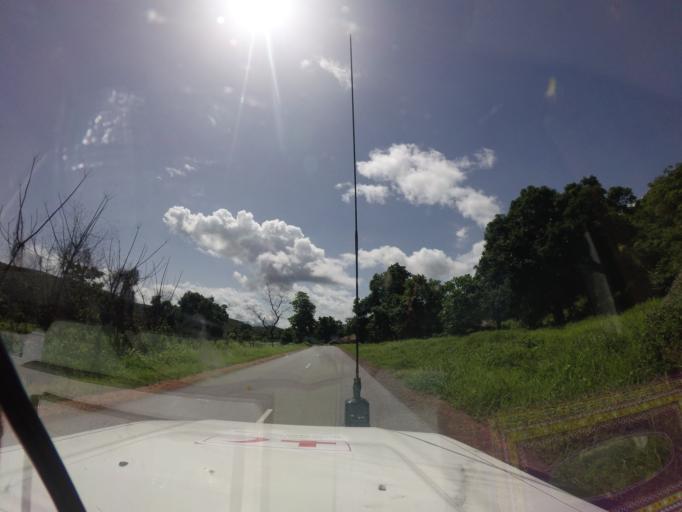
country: GN
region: Mamou
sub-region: Mamou Prefecture
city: Mamou
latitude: 10.2071
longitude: -11.8509
